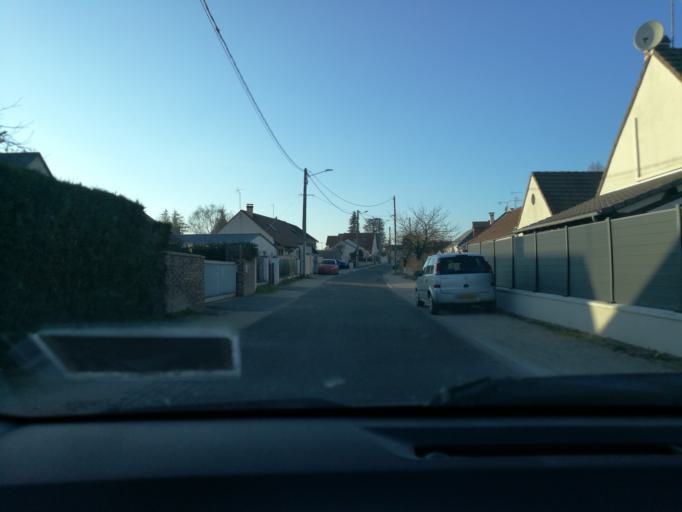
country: FR
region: Centre
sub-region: Departement du Loiret
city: Semoy
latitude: 47.9402
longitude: 1.9452
